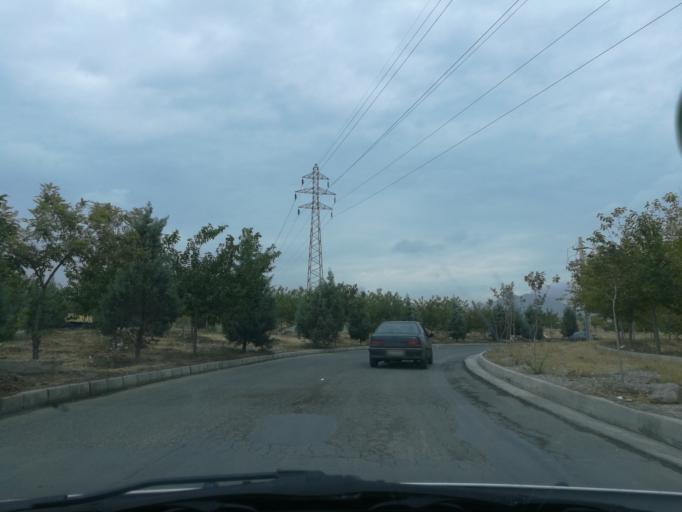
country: IR
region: Alborz
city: Karaj
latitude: 35.8645
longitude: 50.9270
